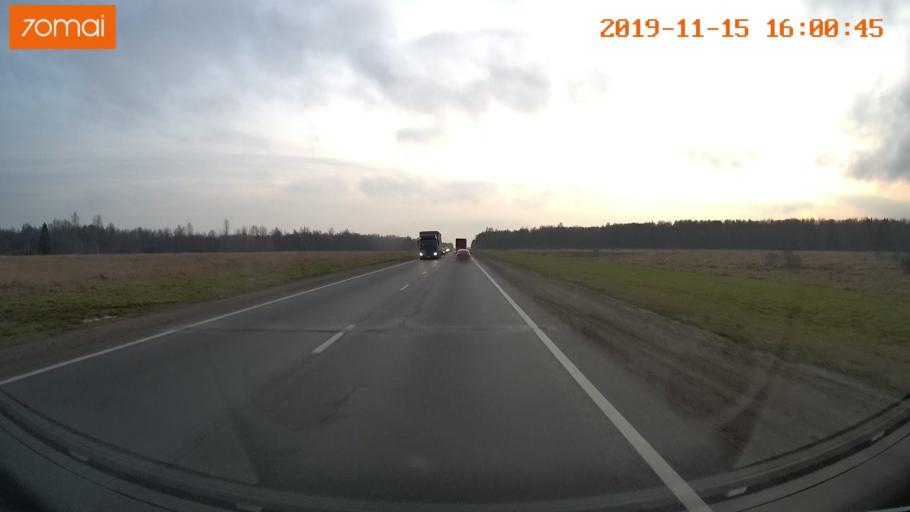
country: RU
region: Jaroslavl
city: Yaroslavl
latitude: 57.7921
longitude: 39.9367
